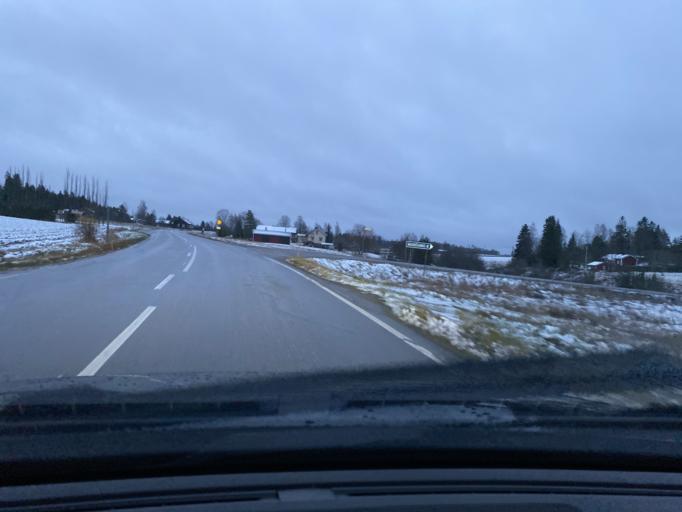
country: FI
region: Pirkanmaa
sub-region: Lounais-Pirkanmaa
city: Punkalaidun
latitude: 61.1235
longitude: 23.0283
